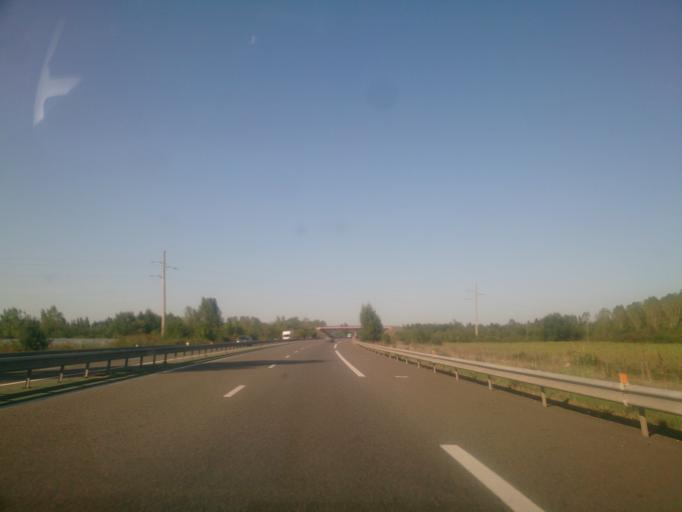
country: FR
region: Midi-Pyrenees
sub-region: Departement du Tarn-et-Garonne
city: Albias
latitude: 44.0890
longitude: 1.4240
